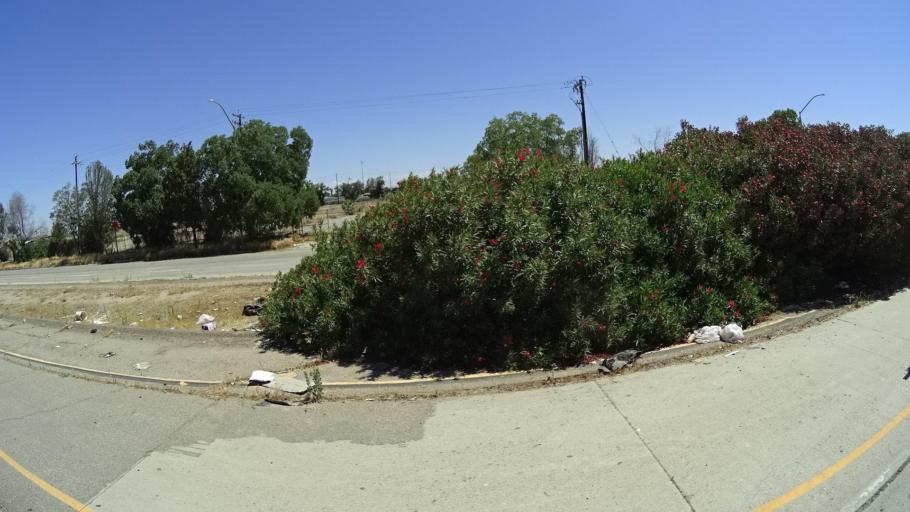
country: US
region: California
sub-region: Fresno County
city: Fresno
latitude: 36.7004
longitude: -119.7621
